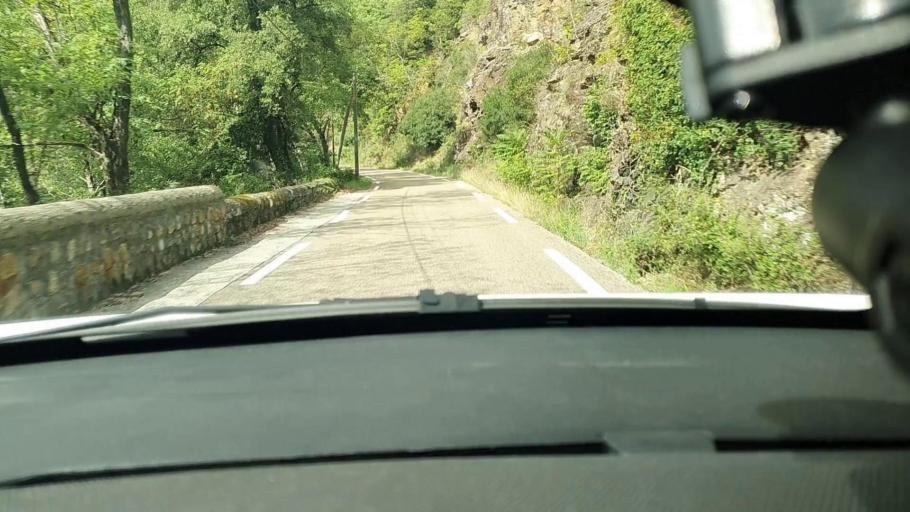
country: FR
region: Languedoc-Roussillon
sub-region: Departement du Gard
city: Branoux-les-Taillades
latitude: 44.3067
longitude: 4.0014
